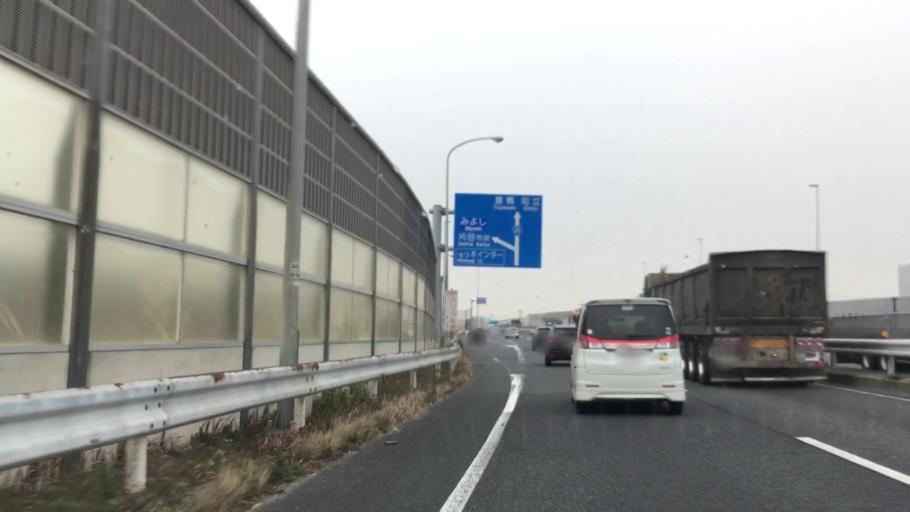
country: JP
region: Aichi
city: Chiryu
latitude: 35.0201
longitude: 137.0136
